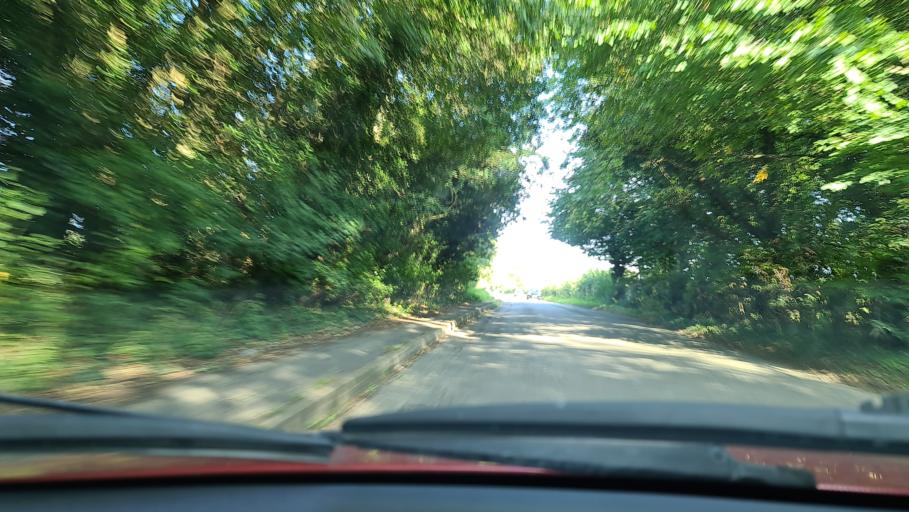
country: GB
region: England
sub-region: Oxfordshire
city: Adderbury
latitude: 52.0220
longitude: -1.2613
